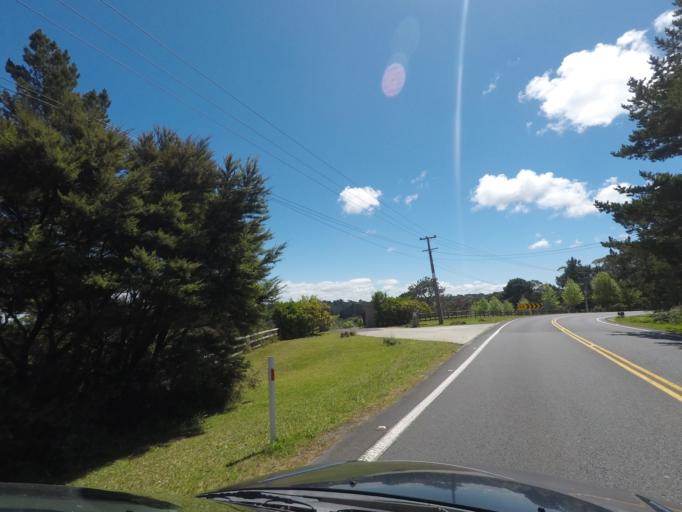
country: NZ
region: Auckland
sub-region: Auckland
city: Rothesay Bay
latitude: -36.7550
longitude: 174.6632
